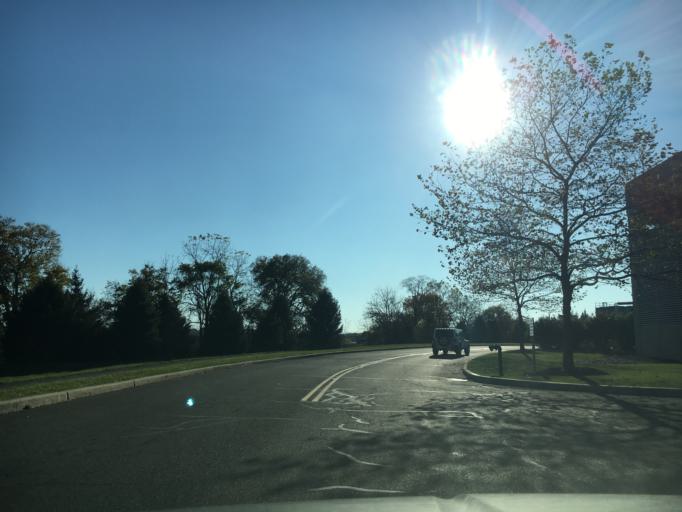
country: US
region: Pennsylvania
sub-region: Lehigh County
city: Fullerton
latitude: 40.6311
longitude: -75.4536
